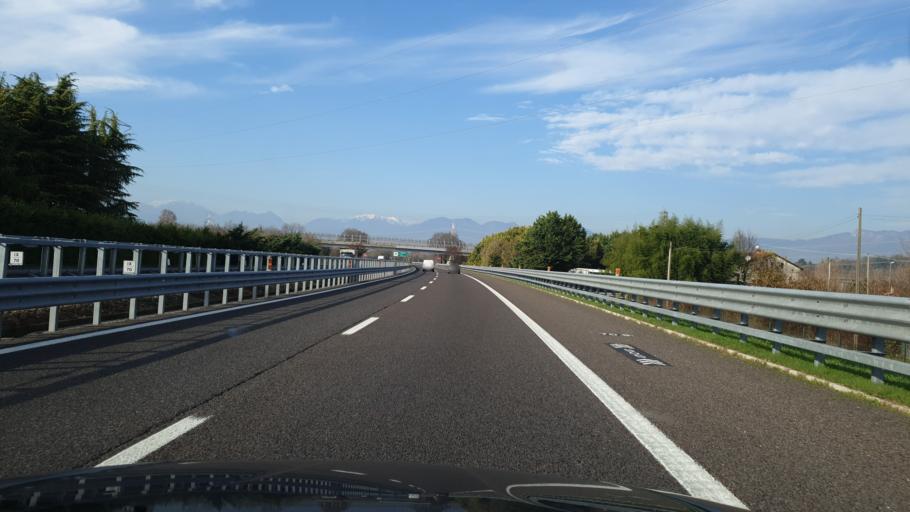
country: IT
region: Veneto
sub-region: Provincia di Vicenza
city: Dueville
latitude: 45.6495
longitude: 11.5571
